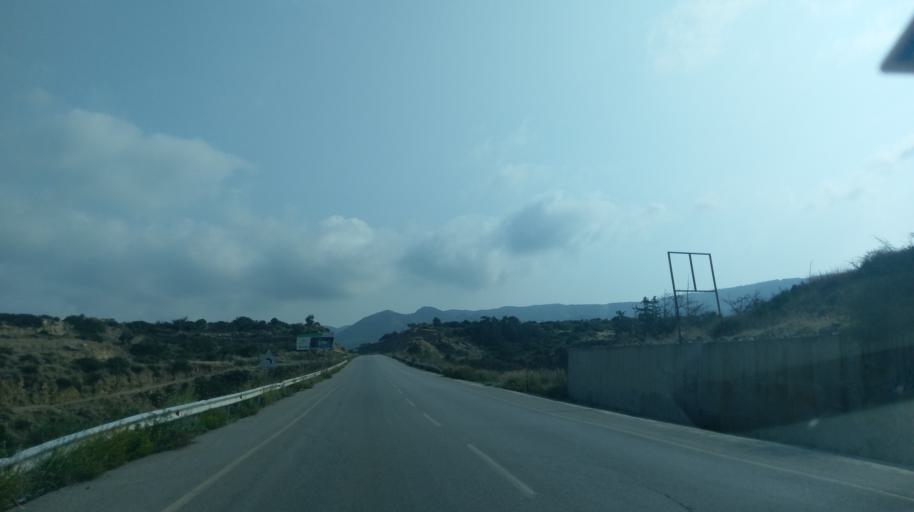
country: CY
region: Ammochostos
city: Lefkonoiko
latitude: 35.3534
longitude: 33.6209
